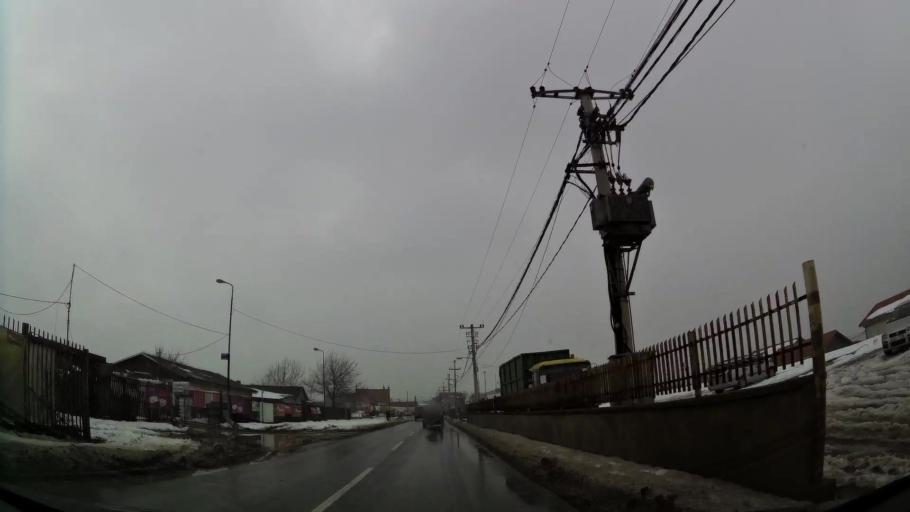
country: RS
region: Central Serbia
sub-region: Belgrade
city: Zvezdara
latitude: 44.7685
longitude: 20.5344
